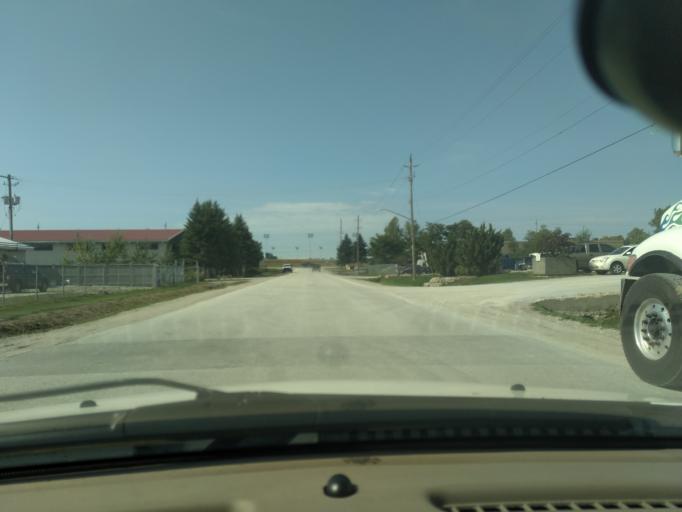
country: CA
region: Ontario
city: Innisfil
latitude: 44.2943
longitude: -79.6790
